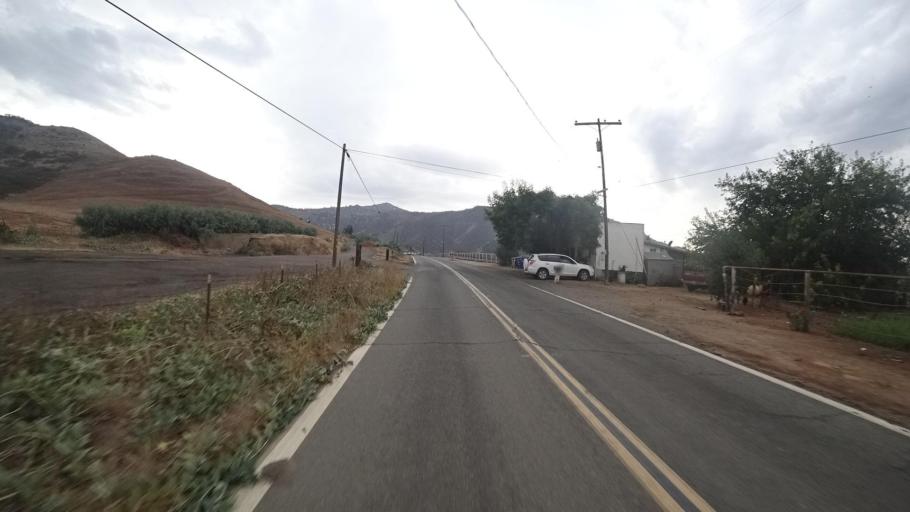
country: US
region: California
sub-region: San Diego County
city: San Pasqual
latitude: 33.0799
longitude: -116.9726
